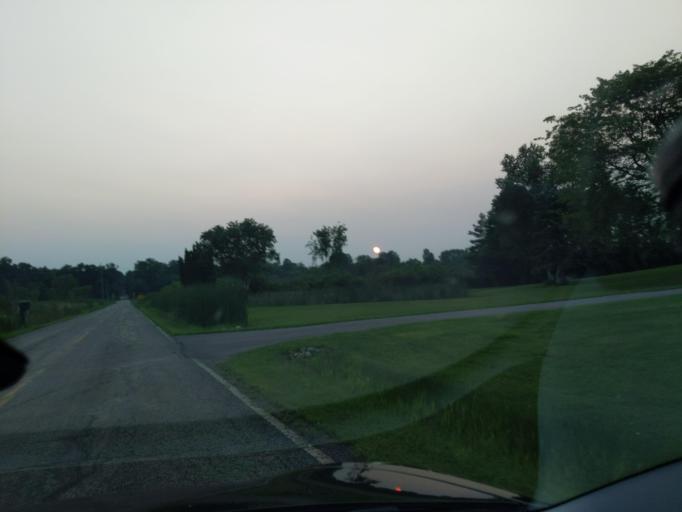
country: US
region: Michigan
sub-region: Ingham County
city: Leslie
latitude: 42.3494
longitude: -84.4435
